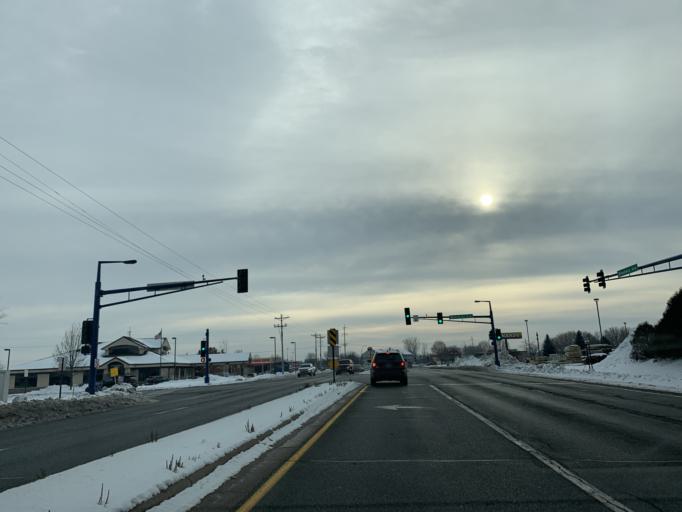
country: US
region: Minnesota
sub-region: Washington County
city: Forest Lake
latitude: 45.2819
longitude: -93.0111
